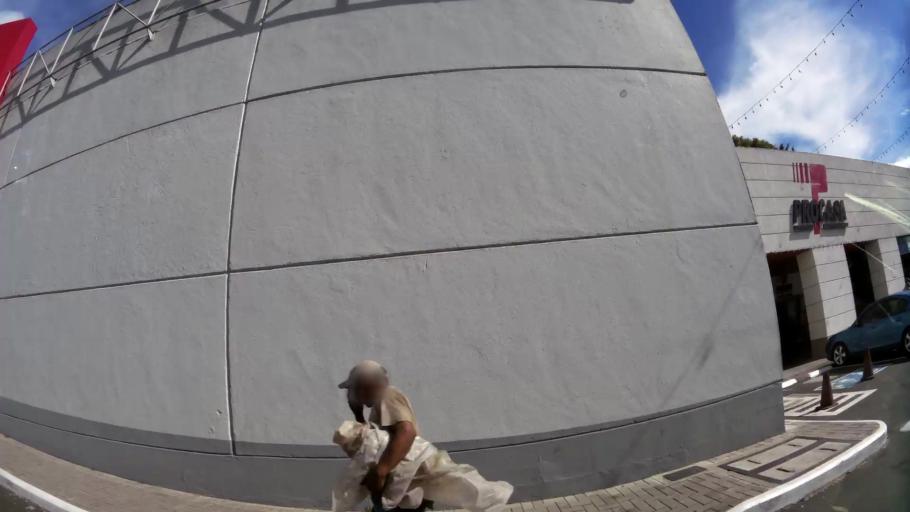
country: GT
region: Guatemala
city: Guatemala City
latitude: 14.6240
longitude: -90.5575
